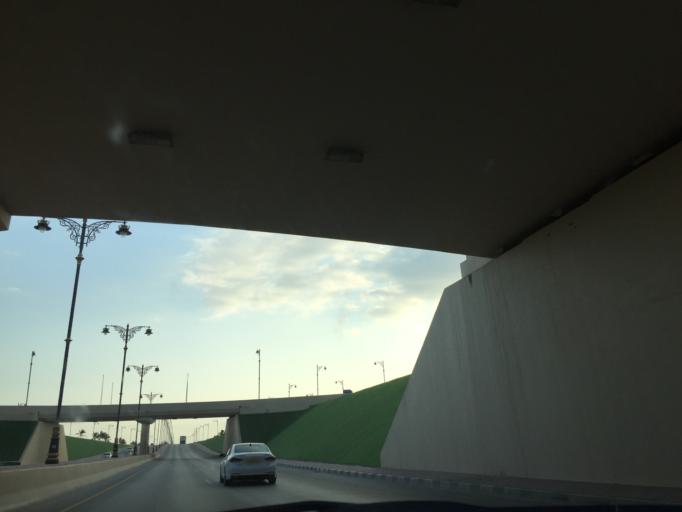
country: OM
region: Zufar
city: Salalah
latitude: 17.0332
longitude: 54.0596
